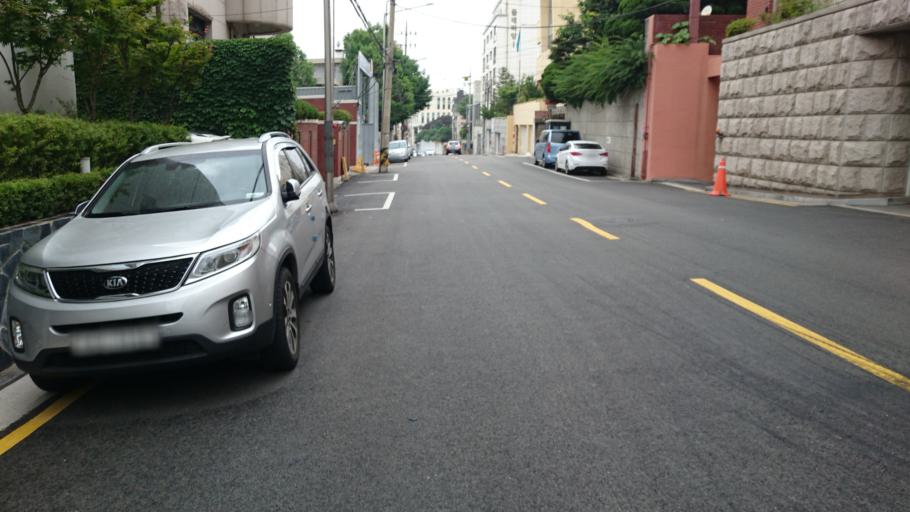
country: KR
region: Seoul
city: Seoul
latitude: 37.5266
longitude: 126.9964
